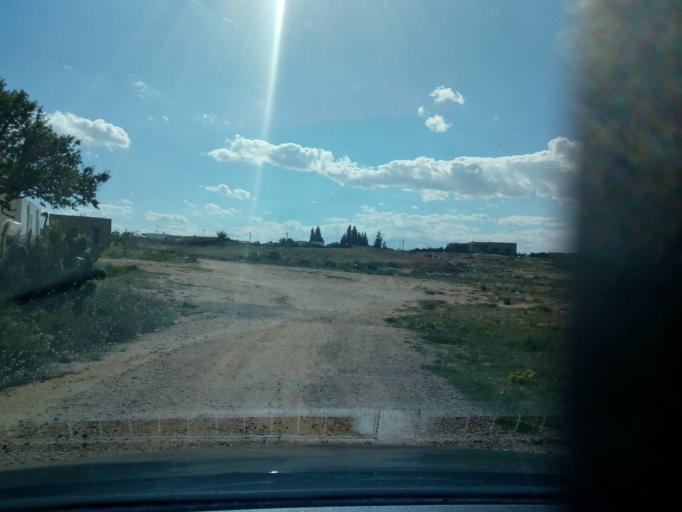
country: TN
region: Safaqis
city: Sfax
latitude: 34.7291
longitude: 10.6039
